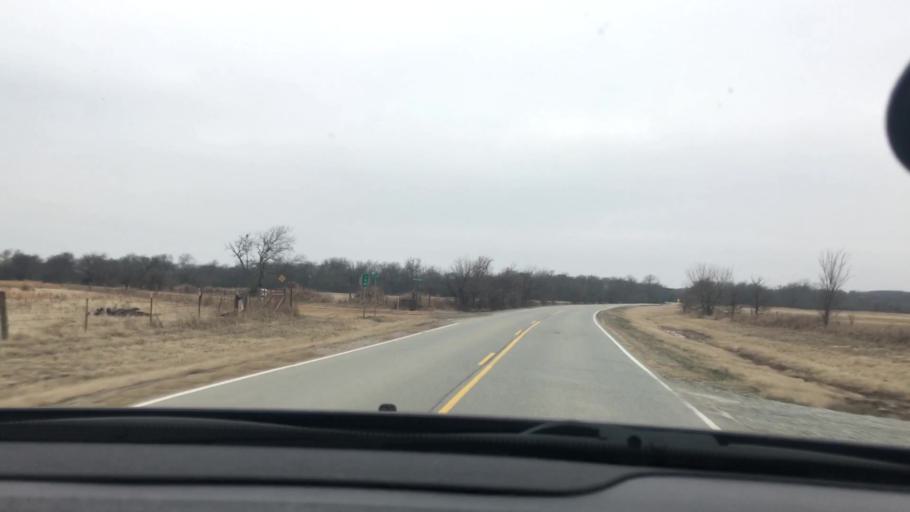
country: US
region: Oklahoma
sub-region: Coal County
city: Coalgate
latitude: 34.5321
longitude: -96.2543
